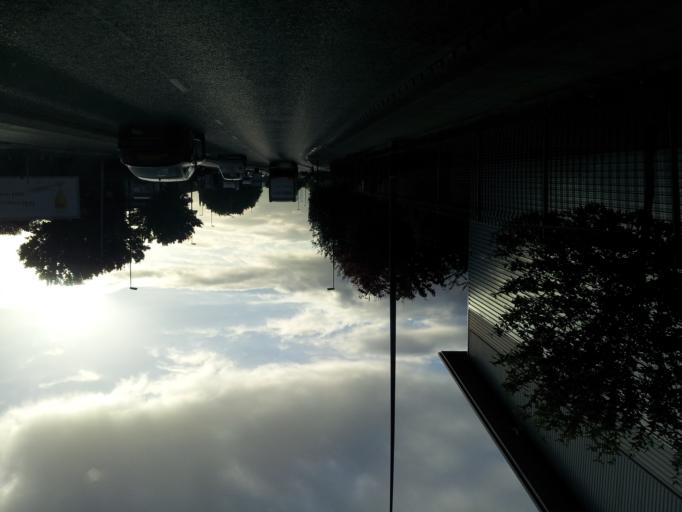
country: GB
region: England
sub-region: Trafford
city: Trafford Park
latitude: 53.4674
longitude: -2.3149
